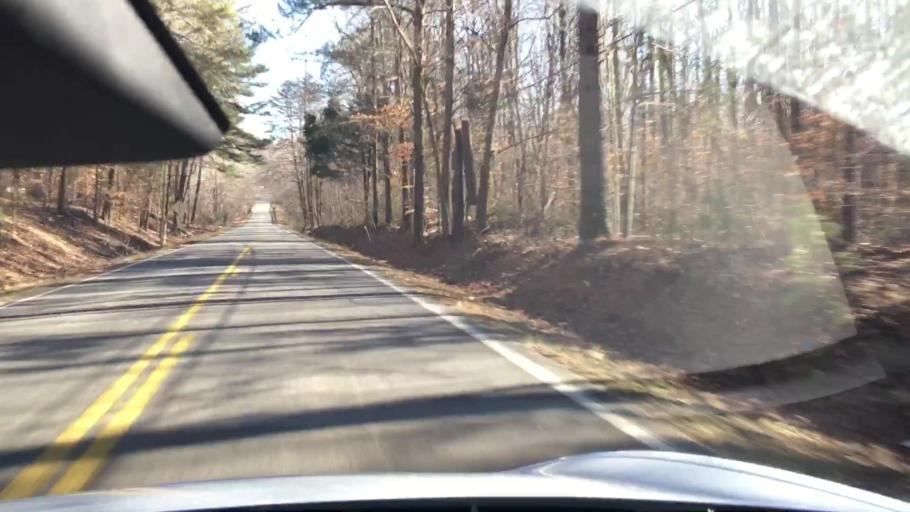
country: US
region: Virginia
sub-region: Henrico County
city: Short Pump
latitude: 37.5783
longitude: -77.7337
